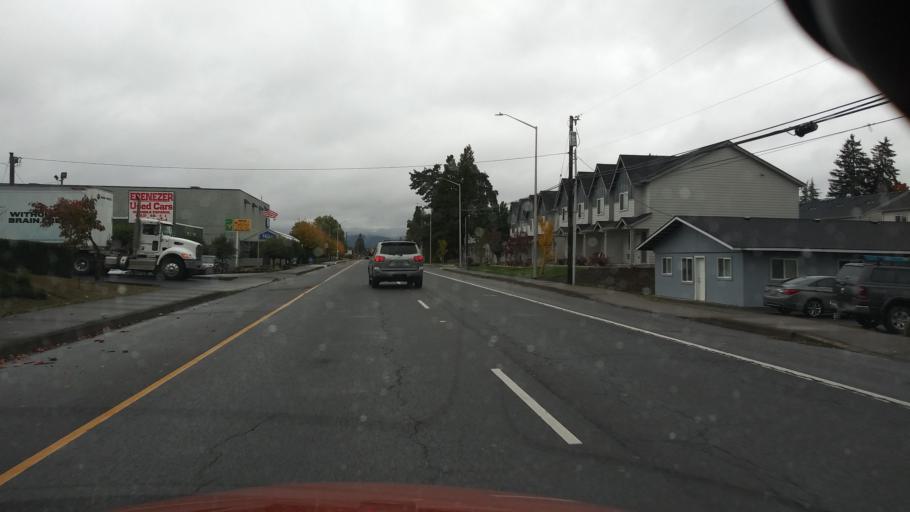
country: US
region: Oregon
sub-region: Washington County
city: Cornelius
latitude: 45.5209
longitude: -123.0615
